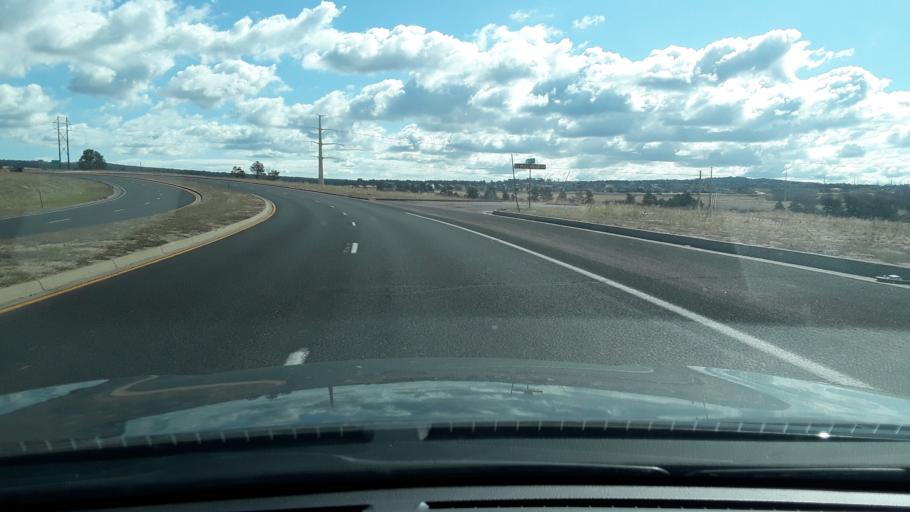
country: US
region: Colorado
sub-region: El Paso County
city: Gleneagle
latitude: 38.9906
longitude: -104.7866
